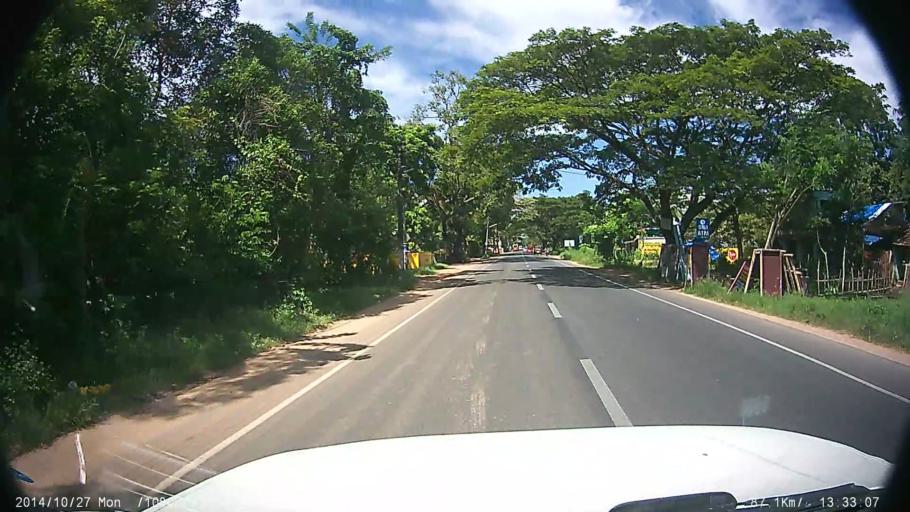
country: IN
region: Kerala
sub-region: Alappuzha
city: Alleppey
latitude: 9.5727
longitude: 76.3275
